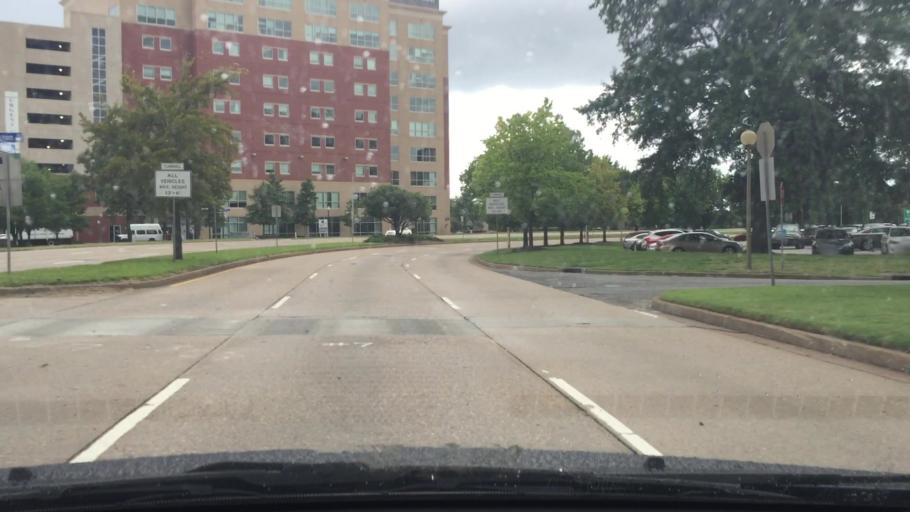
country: US
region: Virginia
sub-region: City of Norfolk
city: Norfolk
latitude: 36.8597
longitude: -76.3050
